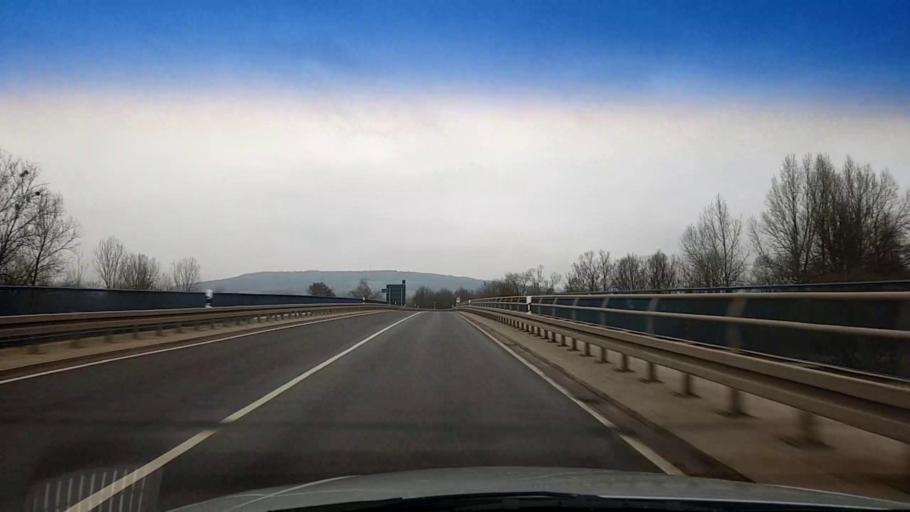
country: DE
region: Bavaria
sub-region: Upper Franconia
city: Breitengussbach
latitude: 49.9807
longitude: 10.8853
